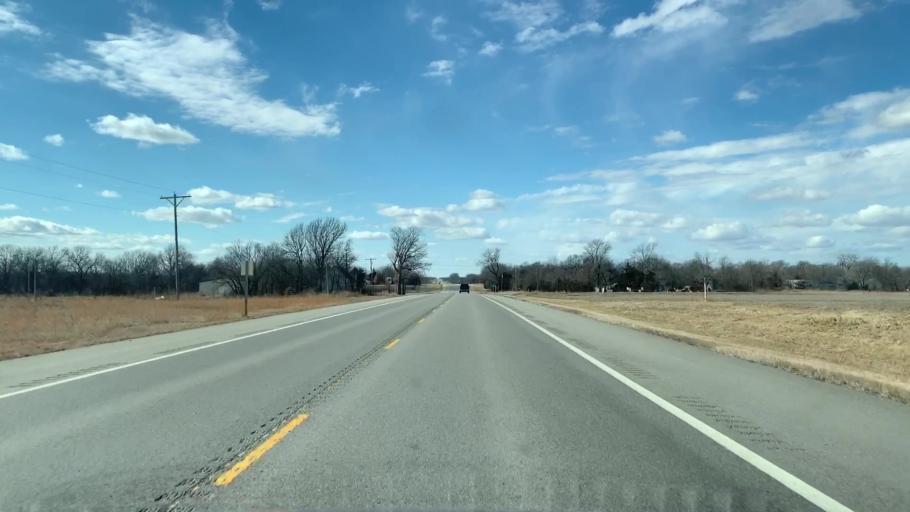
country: US
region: Kansas
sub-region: Labette County
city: Oswego
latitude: 37.3402
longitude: -95.0828
